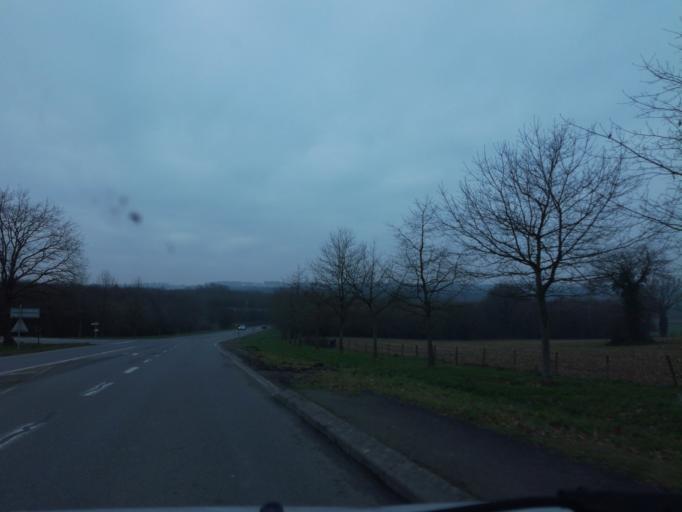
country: FR
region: Brittany
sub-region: Departement d'Ille-et-Vilaine
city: Gosne
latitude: 48.2435
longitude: -1.4610
